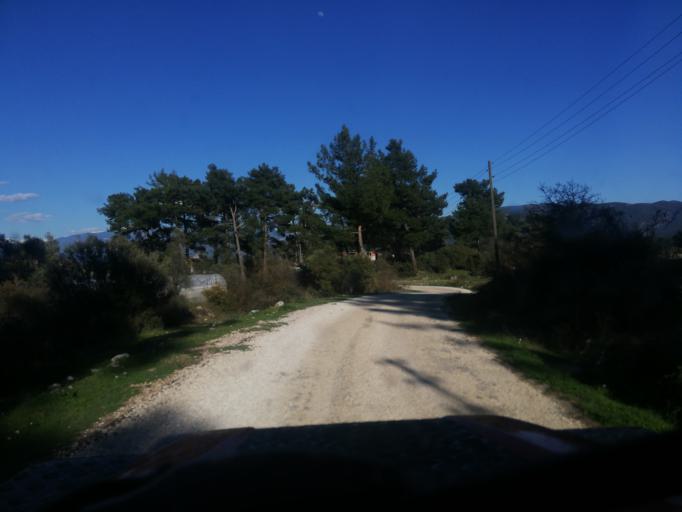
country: TR
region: Antalya
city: Kas
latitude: 36.2979
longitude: 29.6951
